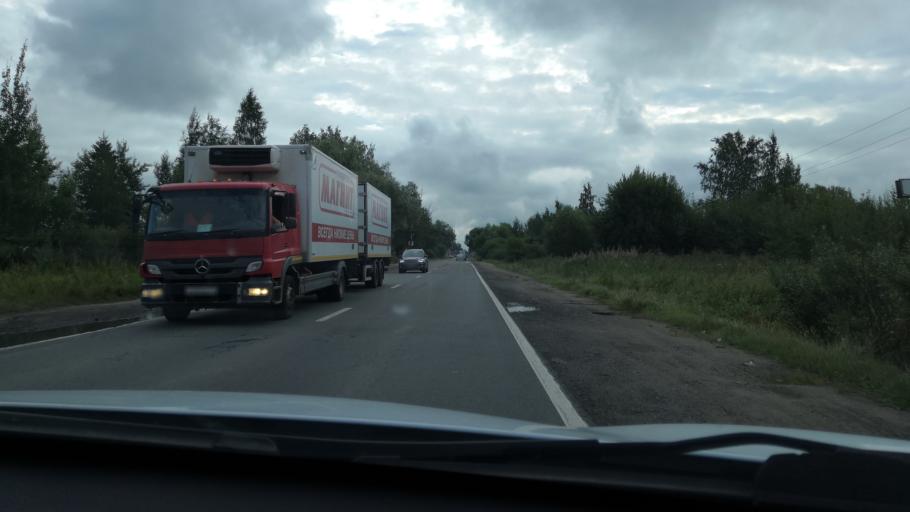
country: RU
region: St.-Petersburg
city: Kolpino
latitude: 59.7048
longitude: 30.5679
